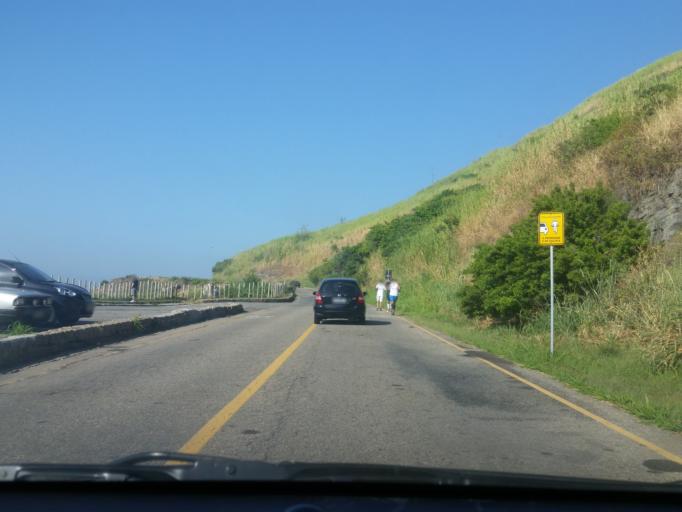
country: BR
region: Rio de Janeiro
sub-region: Nilopolis
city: Nilopolis
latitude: -23.0375
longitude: -43.4995
